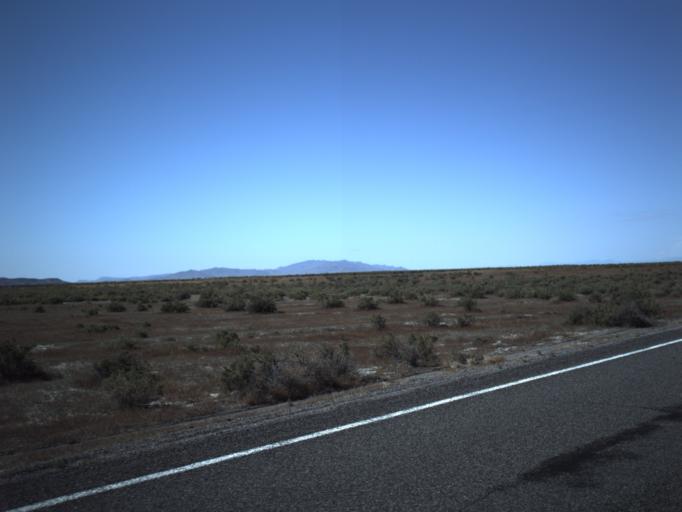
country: US
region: Utah
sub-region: Millard County
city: Delta
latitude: 39.3158
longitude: -112.7503
